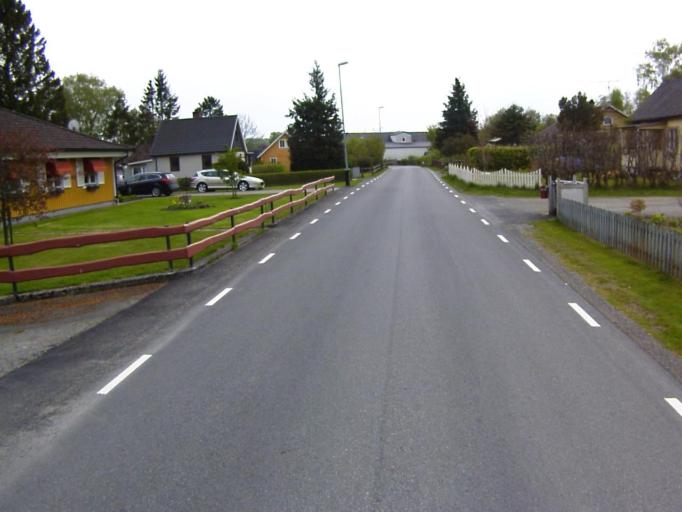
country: SE
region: Skane
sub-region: Kristianstads Kommun
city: Onnestad
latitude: 55.9327
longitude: 13.9555
